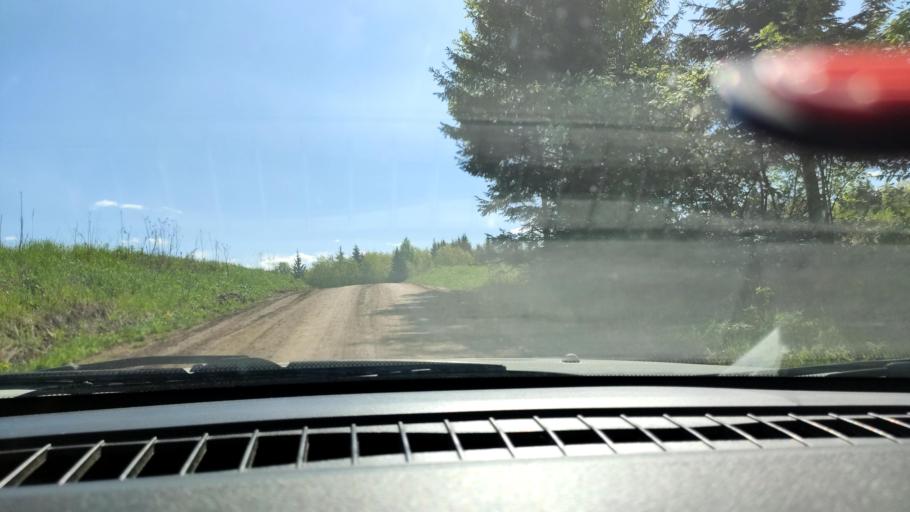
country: RU
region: Perm
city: Bershet'
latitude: 57.7233
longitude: 56.3971
